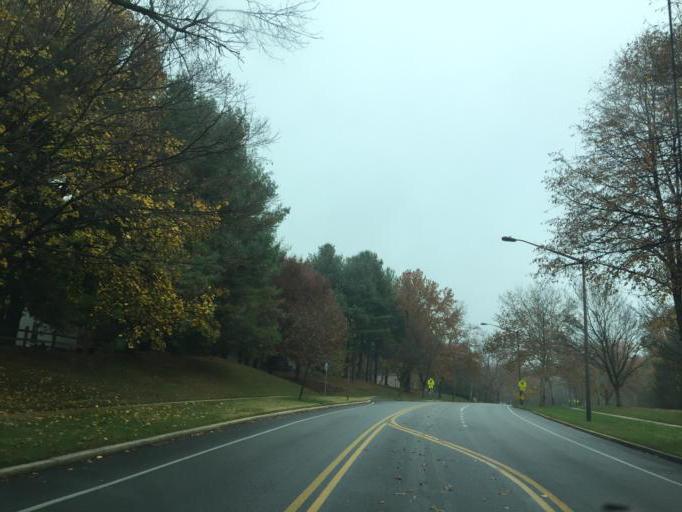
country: US
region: Maryland
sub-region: Howard County
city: Riverside
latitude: 39.1888
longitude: -76.8398
